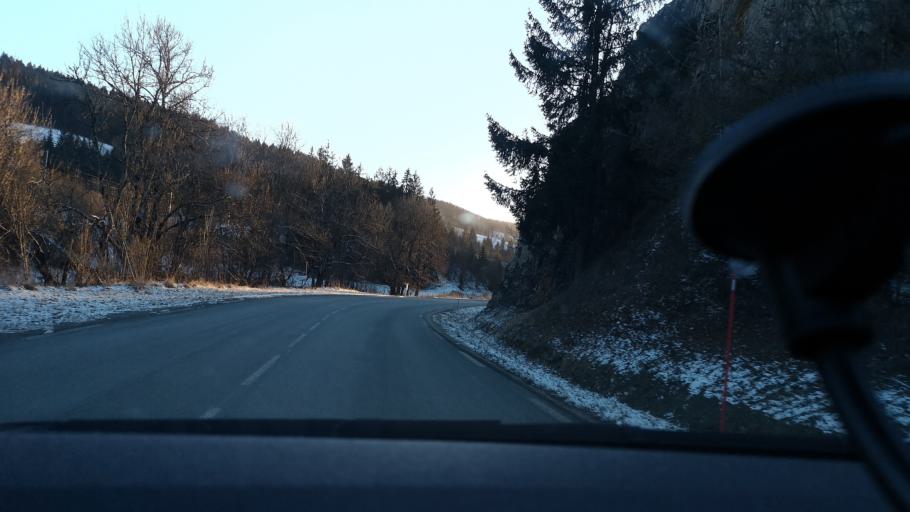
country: FR
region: Franche-Comte
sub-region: Departement du Doubs
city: La Cluse-et-Mijoux
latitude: 46.8855
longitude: 6.4291
